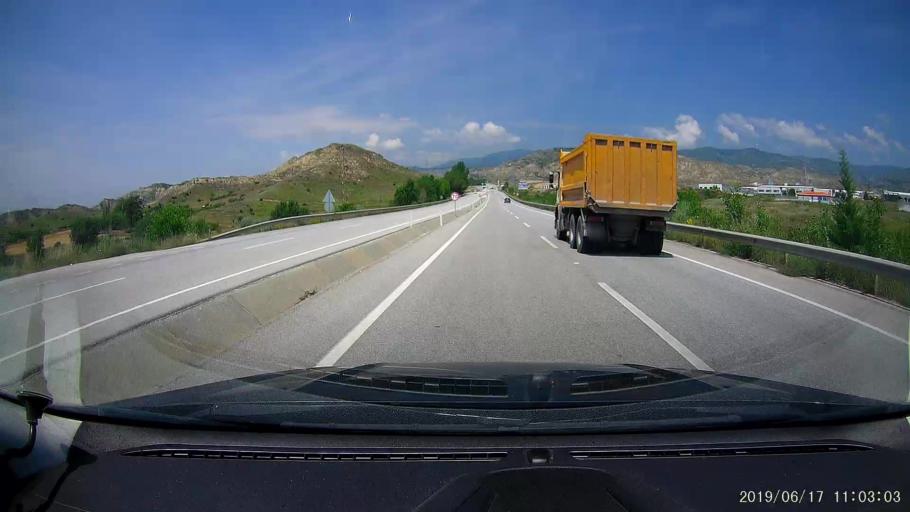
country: TR
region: Kastamonu
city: Tosya
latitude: 41.0157
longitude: 34.1231
